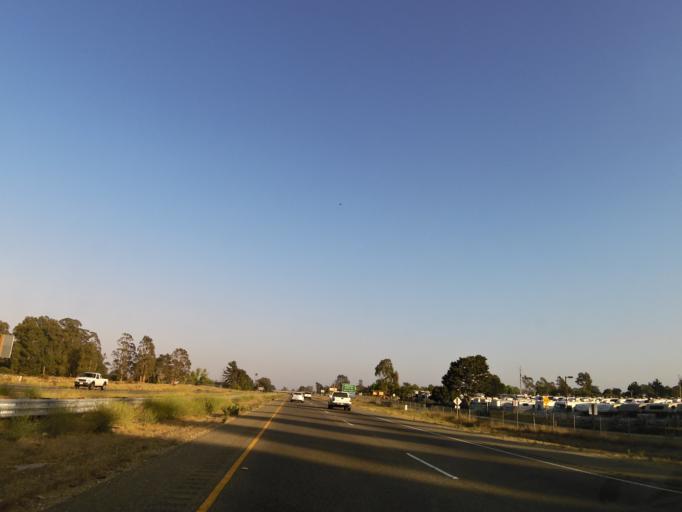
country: US
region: California
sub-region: San Luis Obispo County
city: Nipomo
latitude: 35.0441
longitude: -120.4913
